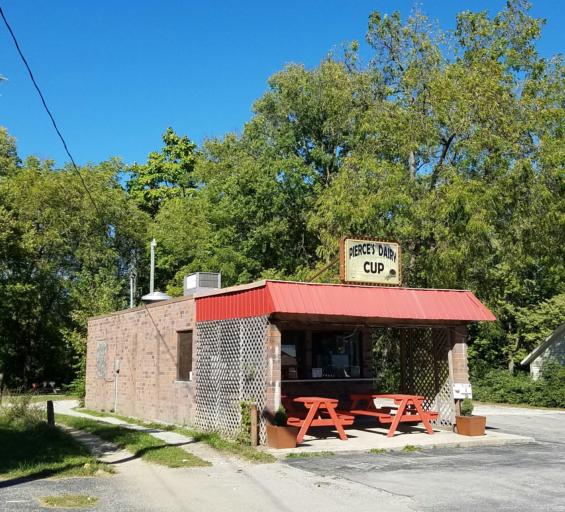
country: US
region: Iowa
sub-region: Decatur County
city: Lamoni
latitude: 40.6237
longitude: -93.9389
